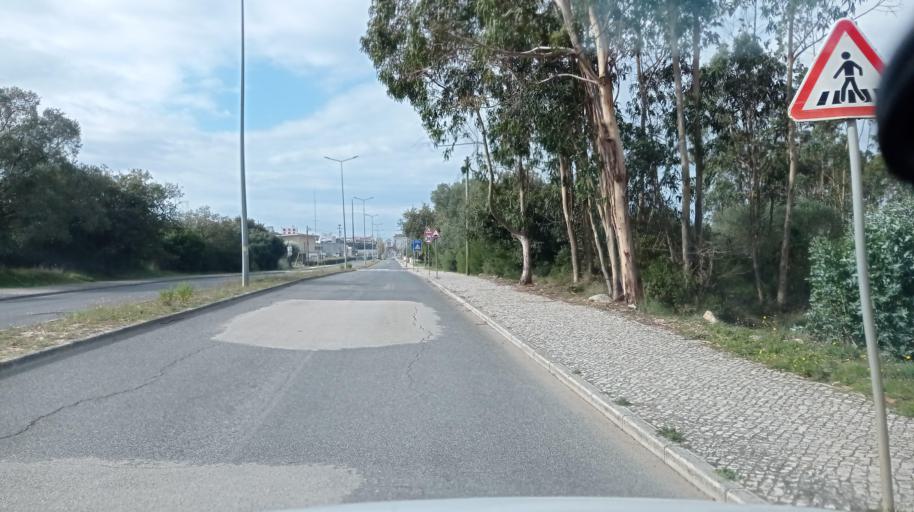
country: PT
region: Leiria
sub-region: Alcobaca
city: Benedita
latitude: 39.4247
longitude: -8.9672
